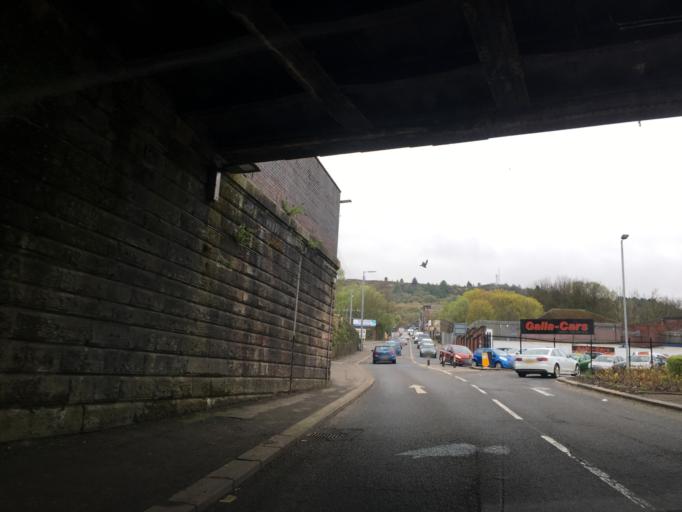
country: GB
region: Scotland
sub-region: Inverclyde
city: Greenock
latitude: 55.9438
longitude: -4.7491
